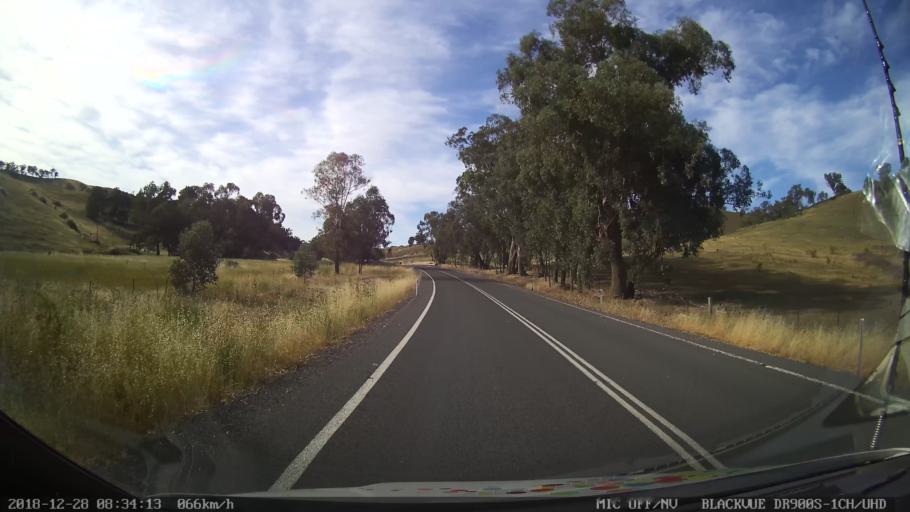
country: AU
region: New South Wales
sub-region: Blayney
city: Blayney
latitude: -33.9727
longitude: 149.3085
